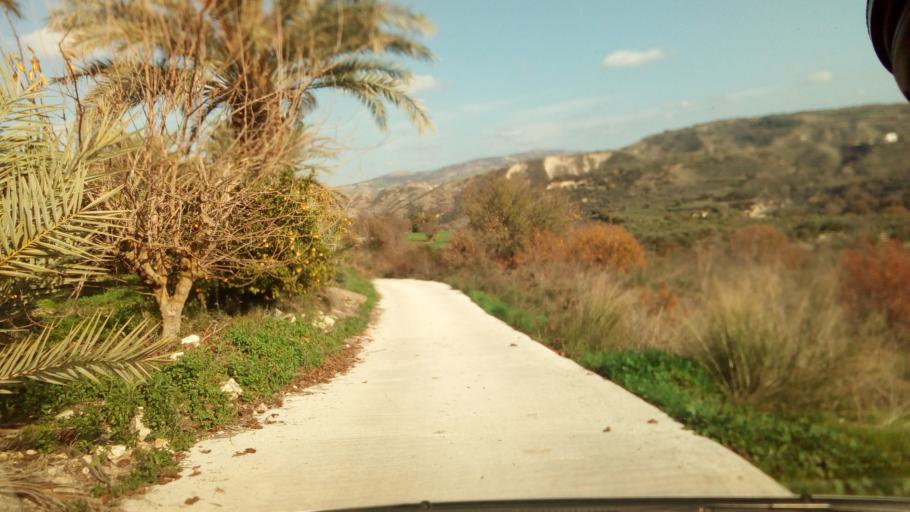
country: CY
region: Pafos
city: Pegeia
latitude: 34.9323
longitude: 32.4661
